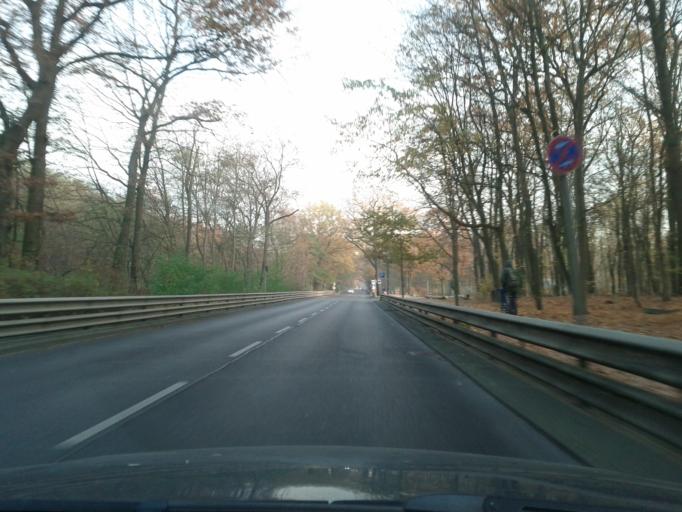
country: DE
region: Berlin
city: Rahnsdorf
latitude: 52.4478
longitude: 13.6693
